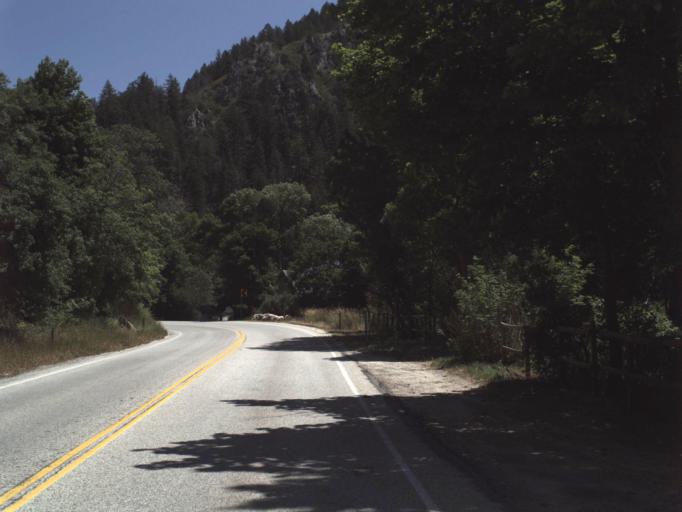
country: US
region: Utah
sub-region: Weber County
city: Liberty
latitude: 41.2542
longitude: -111.8755
